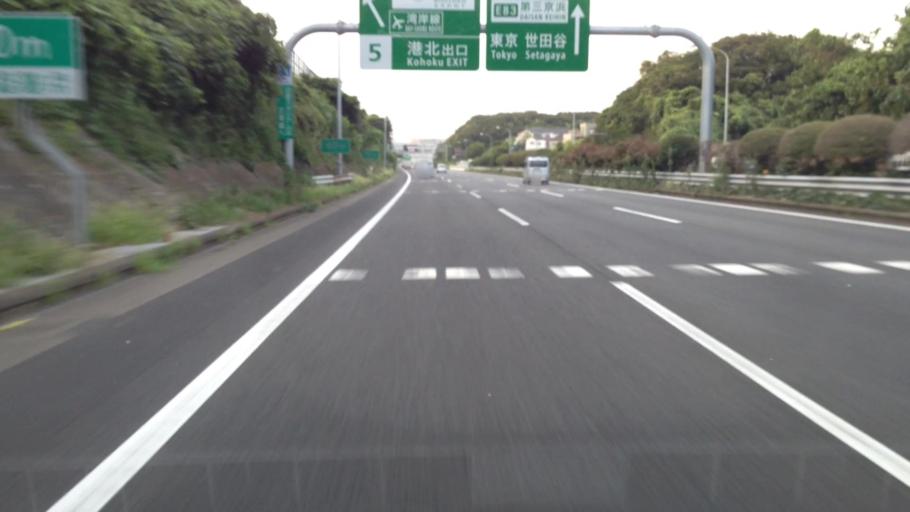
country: JP
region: Kanagawa
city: Yokohama
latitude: 35.5066
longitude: 139.5927
